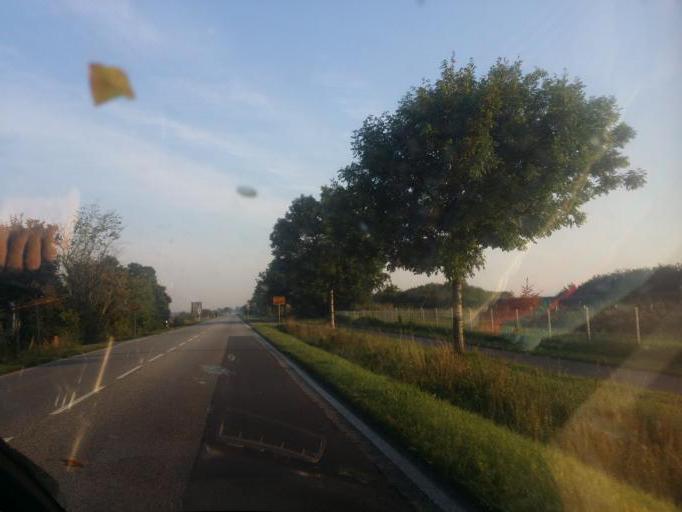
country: DE
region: Schleswig-Holstein
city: Hattstedt
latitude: 54.5323
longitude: 9.0206
